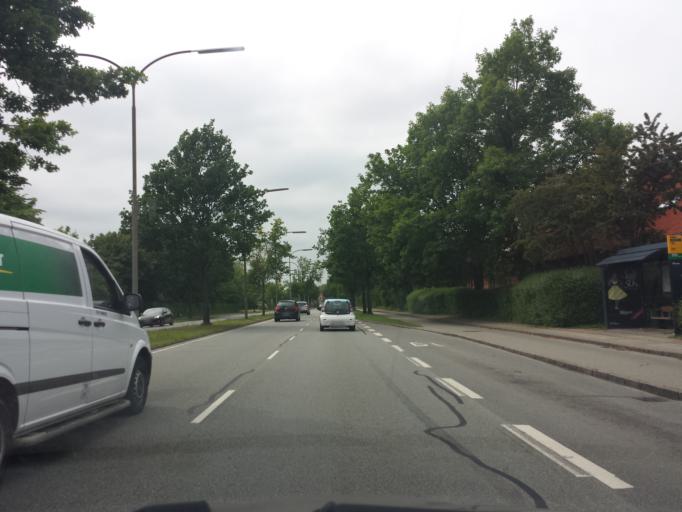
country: DK
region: Capital Region
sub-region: Lyngby-Tarbaek Kommune
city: Kongens Lyngby
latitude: 55.7748
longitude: 12.5210
